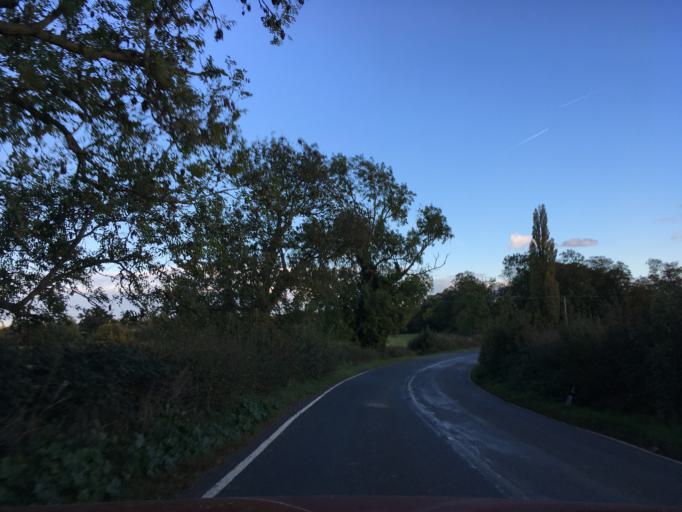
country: GB
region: England
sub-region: Worcestershire
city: Upton upon Severn
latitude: 52.0032
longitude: -2.2619
